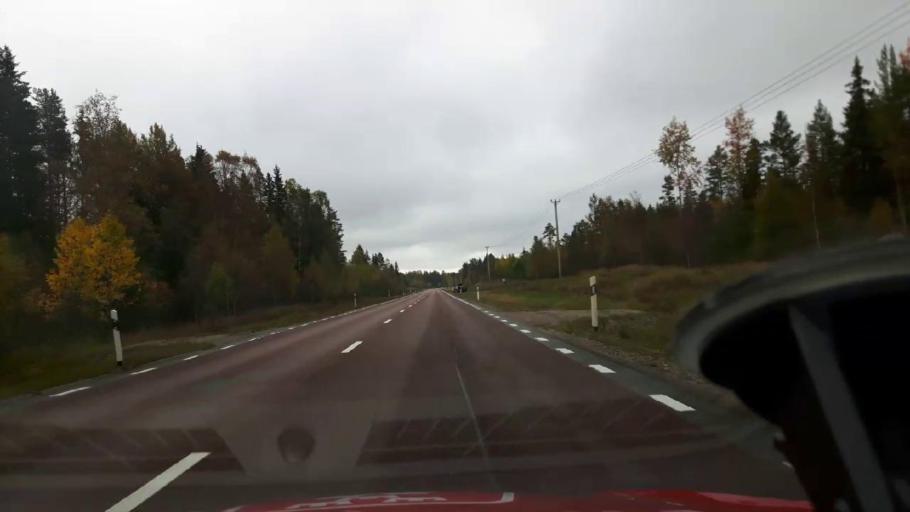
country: SE
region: Jaemtland
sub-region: Harjedalens Kommun
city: Sveg
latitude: 62.2662
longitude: 14.8079
